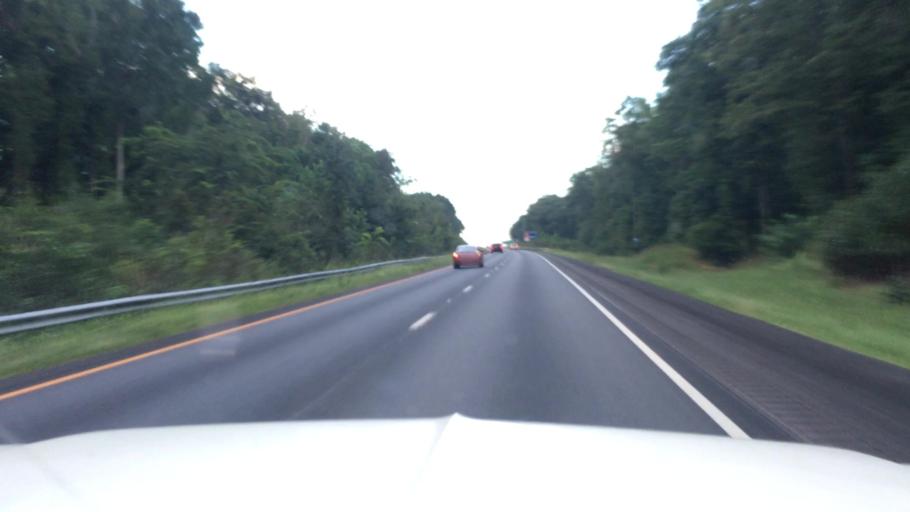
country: US
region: Alabama
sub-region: Chilton County
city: Jemison
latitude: 32.9921
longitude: -86.6968
